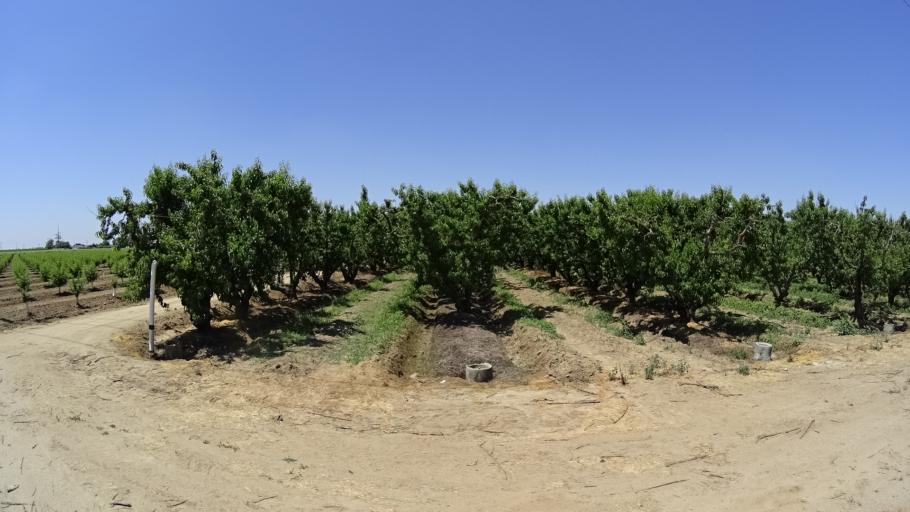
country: US
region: California
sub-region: Fresno County
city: Kingsburg
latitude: 36.4780
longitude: -119.5821
